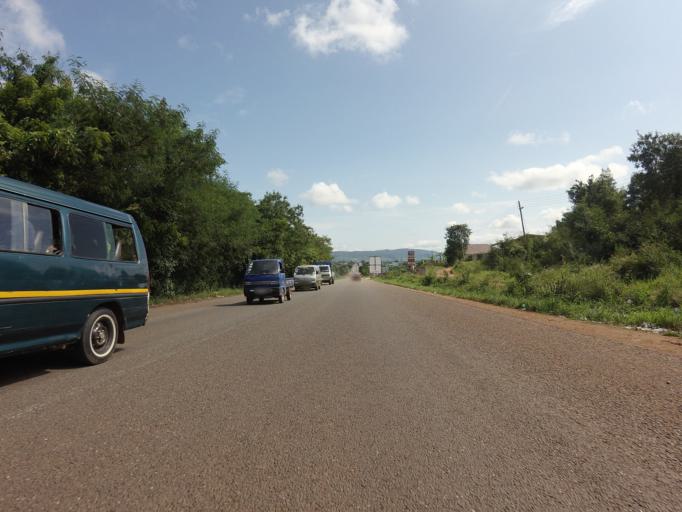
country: GH
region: Eastern
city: Aburi
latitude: 5.8262
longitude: -0.1191
